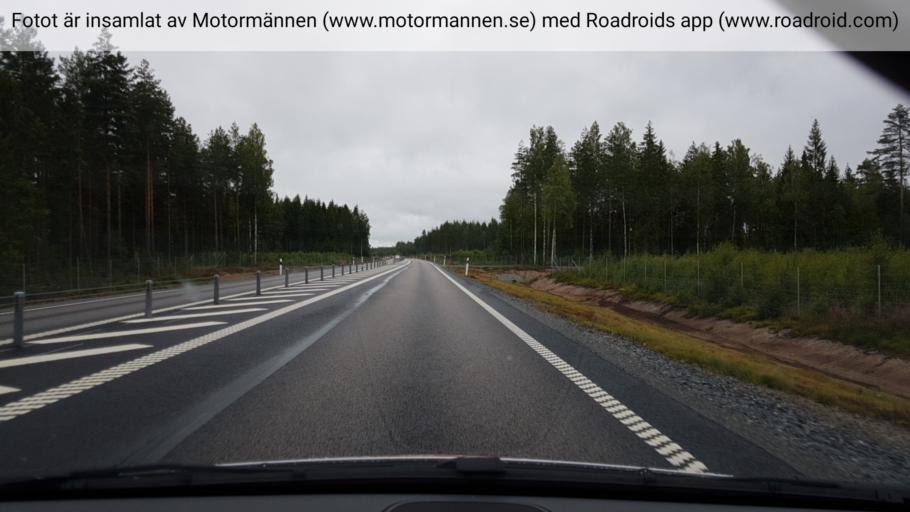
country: SE
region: Uppsala
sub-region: Heby Kommun
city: Tarnsjo
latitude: 60.0737
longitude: 16.9104
